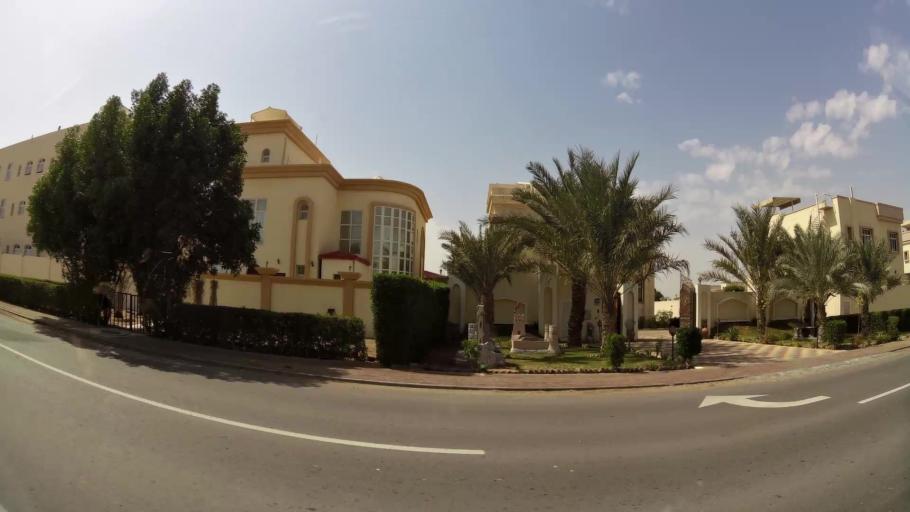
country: AE
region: Abu Dhabi
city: Abu Dhabi
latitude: 24.3136
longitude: 54.5747
